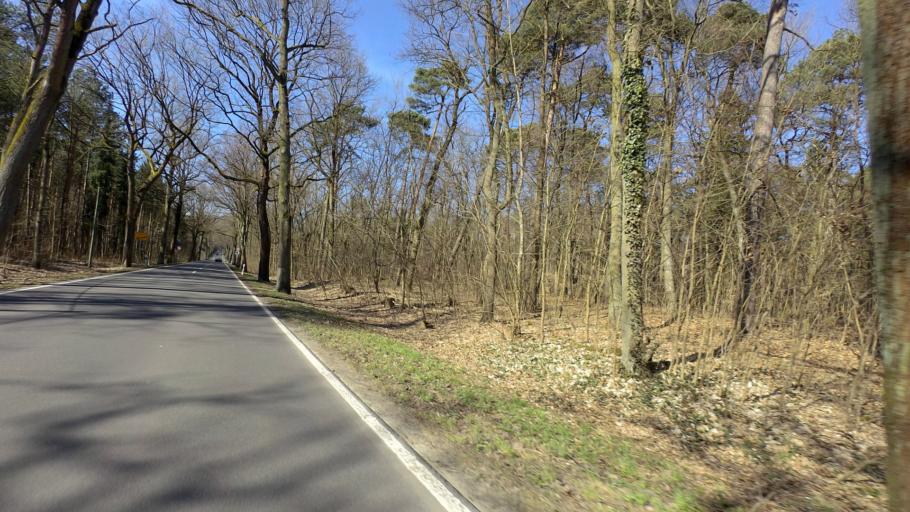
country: DE
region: Brandenburg
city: Waldsieversdorf
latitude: 52.5423
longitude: 14.0532
